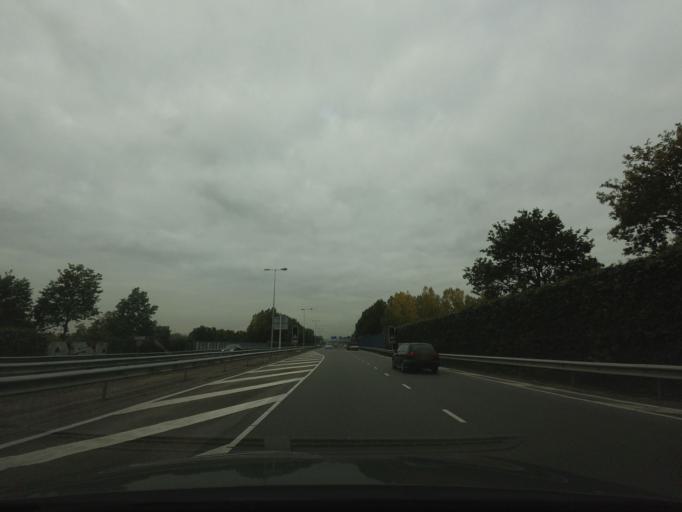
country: NL
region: North Holland
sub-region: Gemeente Ouder-Amstel
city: Duivendrecht
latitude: 52.3340
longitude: 4.9474
